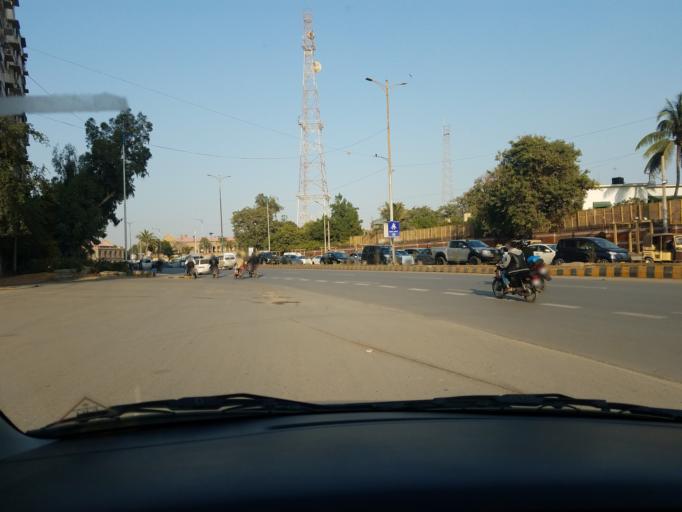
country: PK
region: Sindh
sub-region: Karachi District
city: Karachi
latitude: 24.8528
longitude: 67.0346
